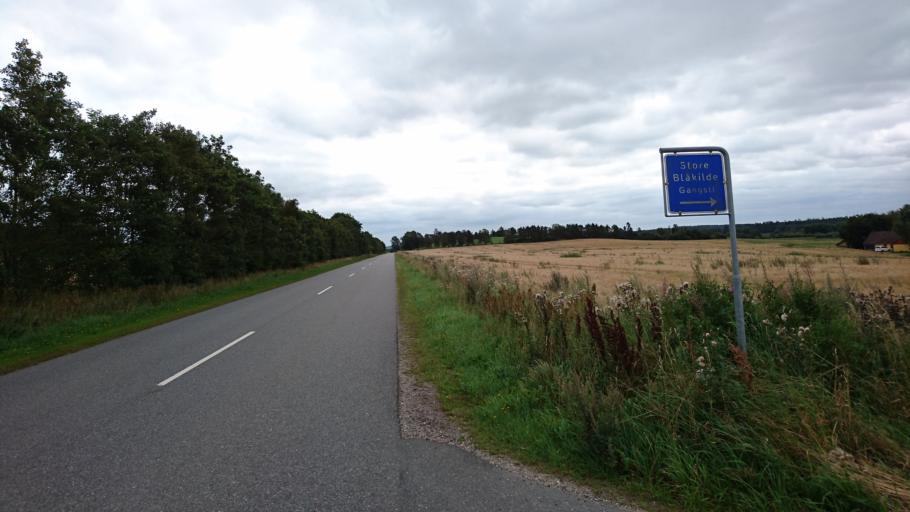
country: DK
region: North Denmark
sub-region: Rebild Kommune
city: Skorping
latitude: 56.7838
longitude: 9.9253
